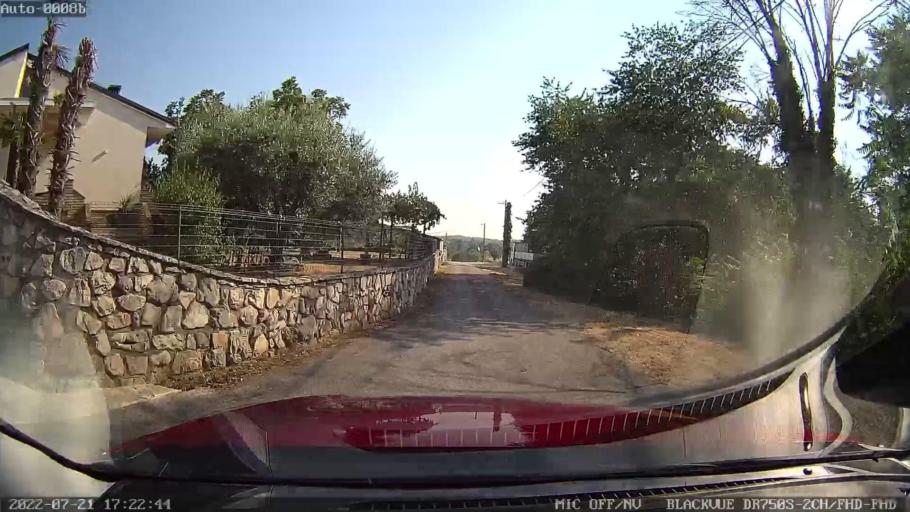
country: HR
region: Istarska
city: Karojba
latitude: 45.1891
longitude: 13.8293
